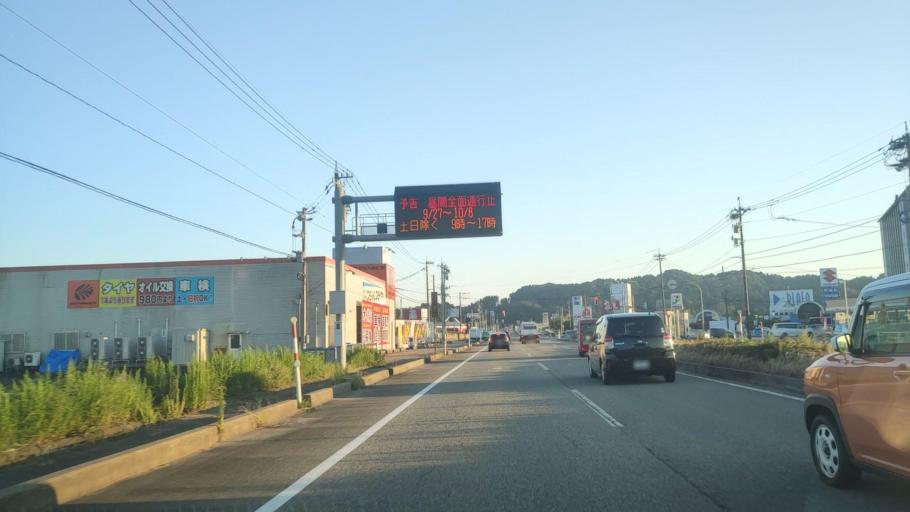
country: JP
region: Toyama
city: Himi
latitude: 36.8652
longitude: 136.9756
